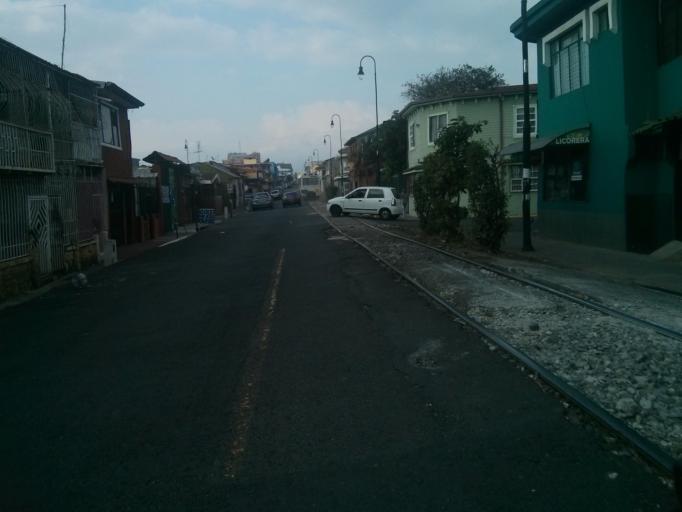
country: CR
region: San Jose
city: San Jose
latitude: 9.9266
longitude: -84.0734
